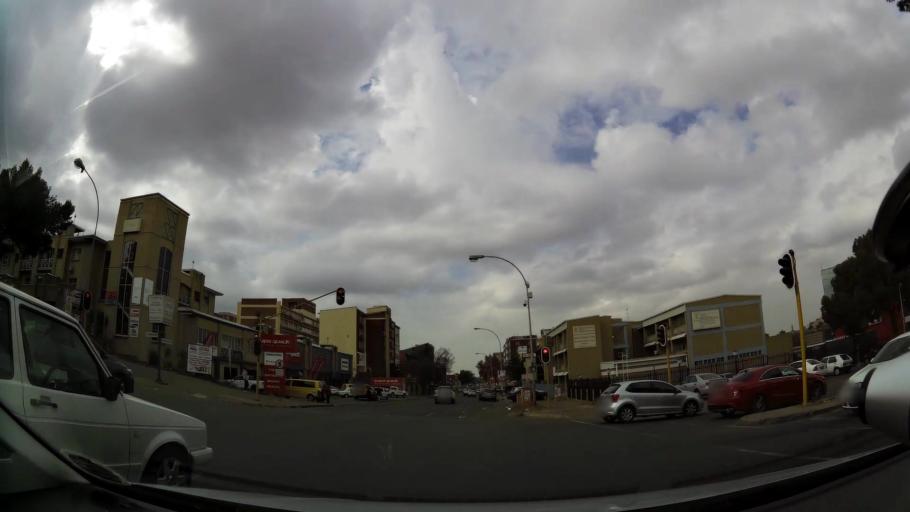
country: ZA
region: Orange Free State
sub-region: Mangaung Metropolitan Municipality
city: Bloemfontein
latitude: -29.1124
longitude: 26.2151
